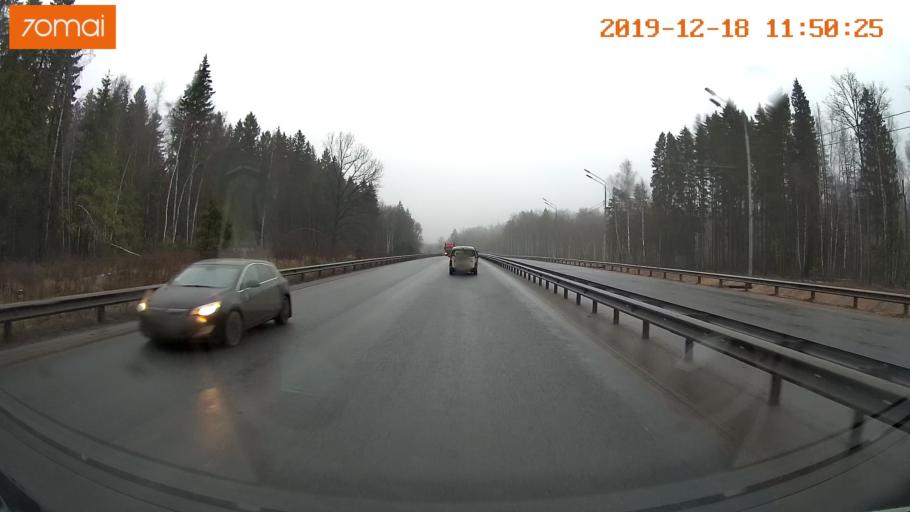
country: RU
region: Moskovskaya
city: Yershovo
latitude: 55.7856
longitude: 36.9186
